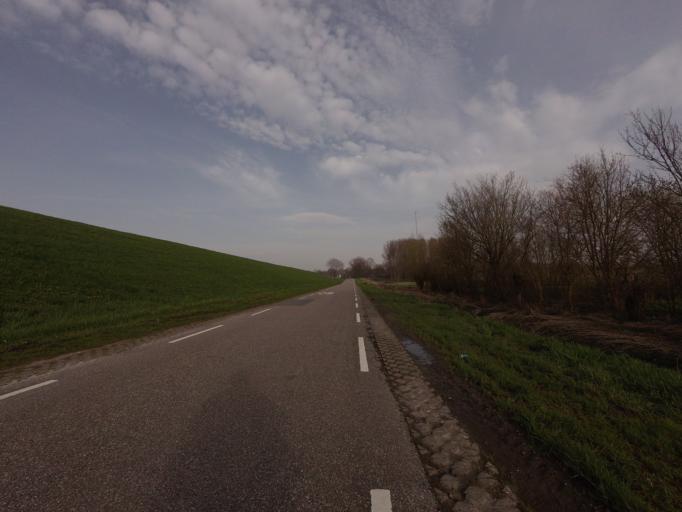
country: NL
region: Zeeland
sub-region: Gemeente Terneuzen
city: Zaamslag
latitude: 51.3646
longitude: 3.9546
